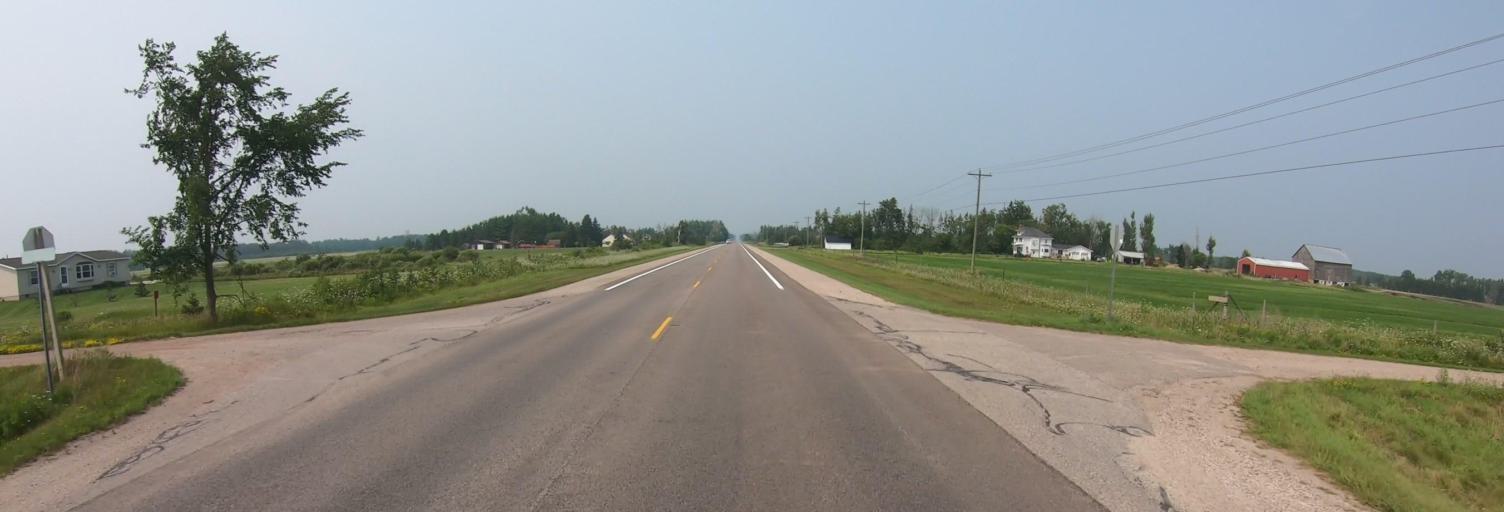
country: US
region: Michigan
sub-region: Chippewa County
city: Sault Ste. Marie
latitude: 46.1727
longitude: -84.3636
